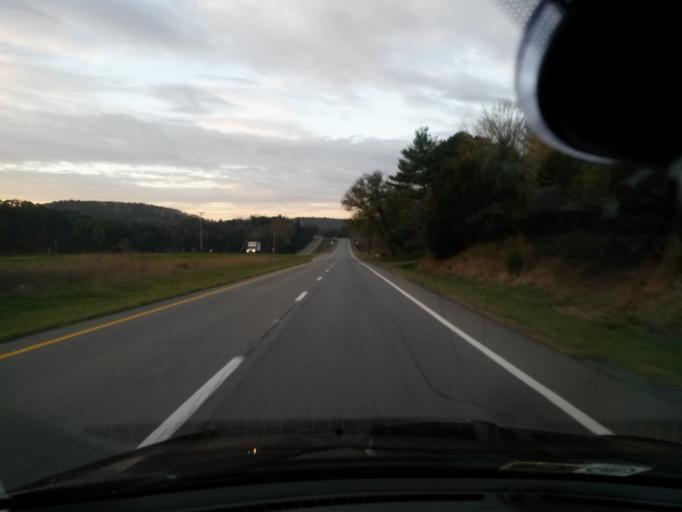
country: US
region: Virginia
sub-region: Botetourt County
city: Fincastle
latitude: 37.5260
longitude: -79.8748
